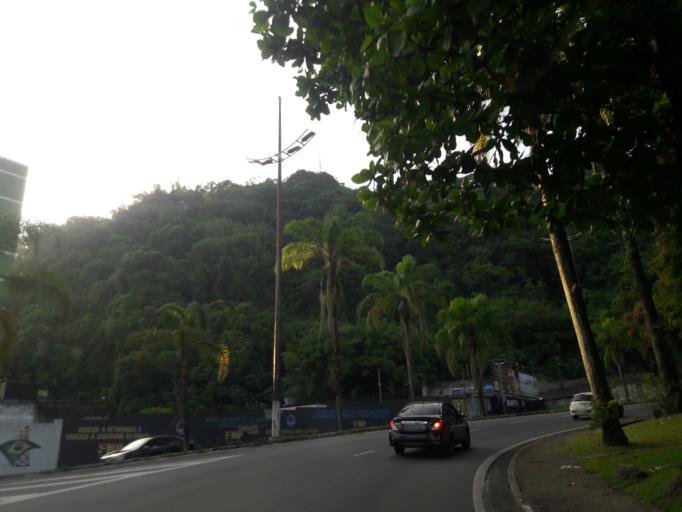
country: BR
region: Sao Paulo
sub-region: Santos
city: Santos
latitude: -23.9364
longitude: -46.3318
